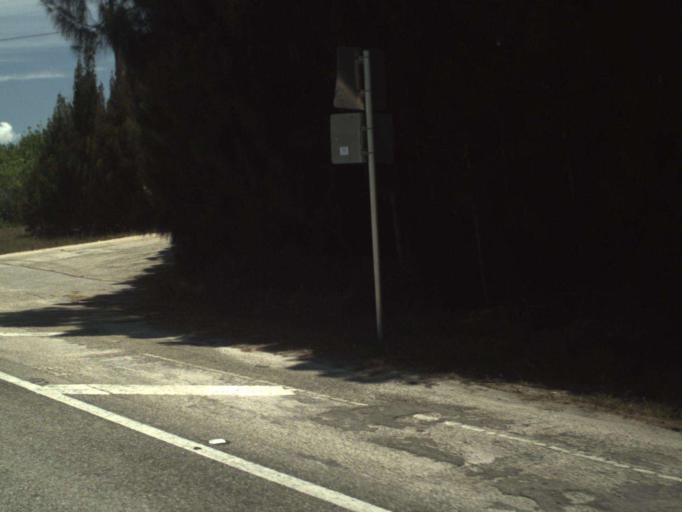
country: US
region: Florida
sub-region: Saint Lucie County
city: Fort Pierce North
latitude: 27.4937
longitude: -80.3440
